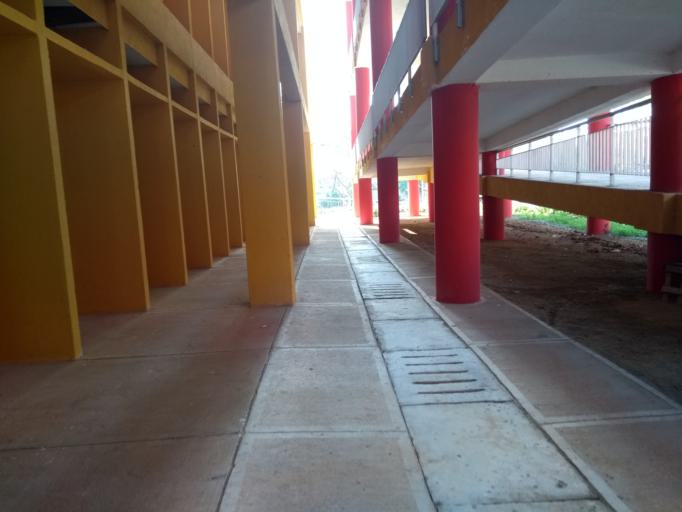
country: CO
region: La Guajira
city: Riohacha
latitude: 11.5119
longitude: -72.8710
